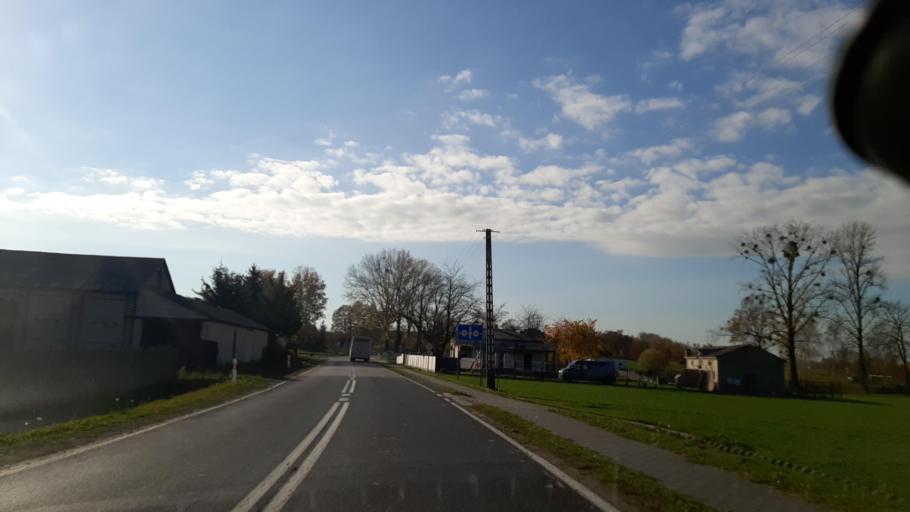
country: PL
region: Lublin Voivodeship
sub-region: Powiat lubelski
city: Jastkow
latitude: 51.3444
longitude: 22.4132
